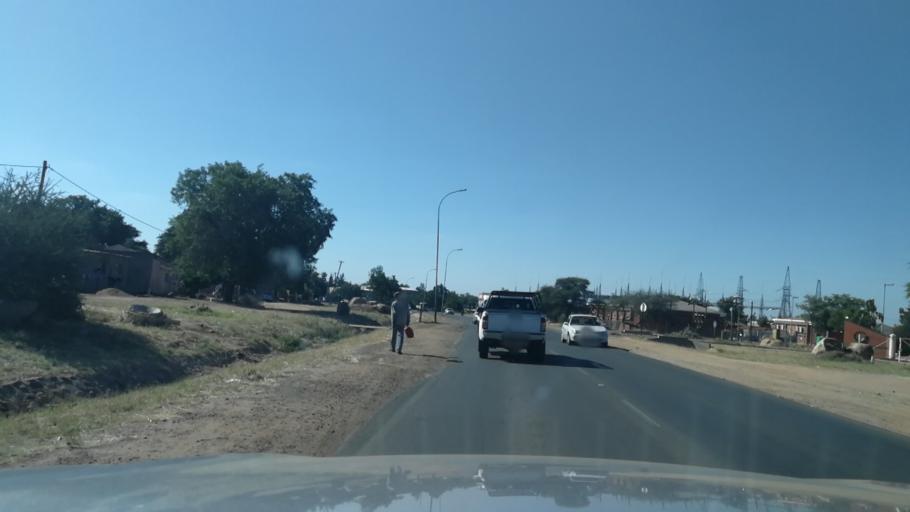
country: BW
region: South East
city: Gaborone
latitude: -24.6878
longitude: 25.9036
